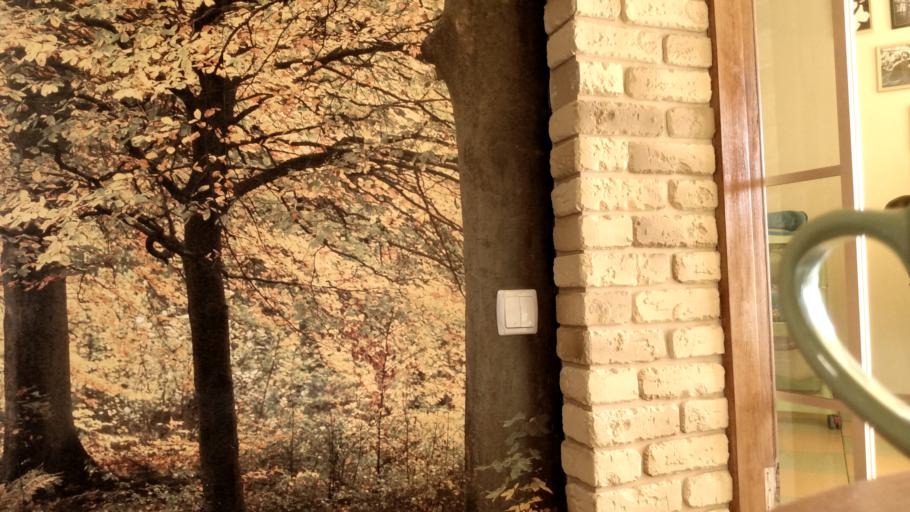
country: RU
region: Vologda
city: Imeni Zhelyabova
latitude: 58.8209
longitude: 36.8762
